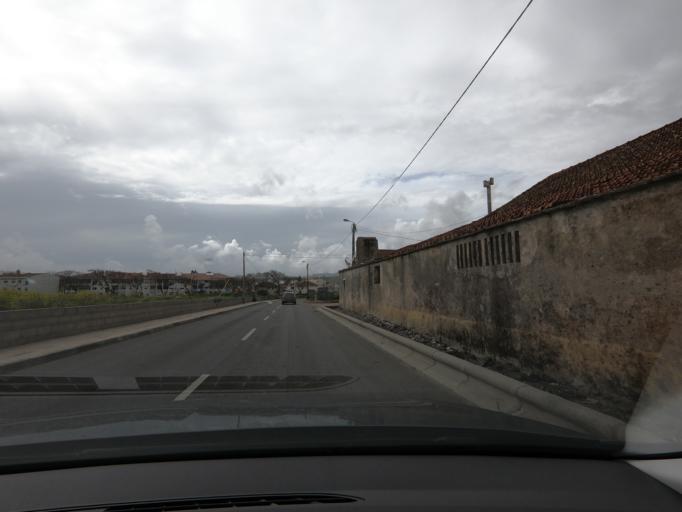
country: PT
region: Lisbon
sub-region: Cascais
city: Sao Domingos de Rana
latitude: 38.7354
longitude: -9.3344
